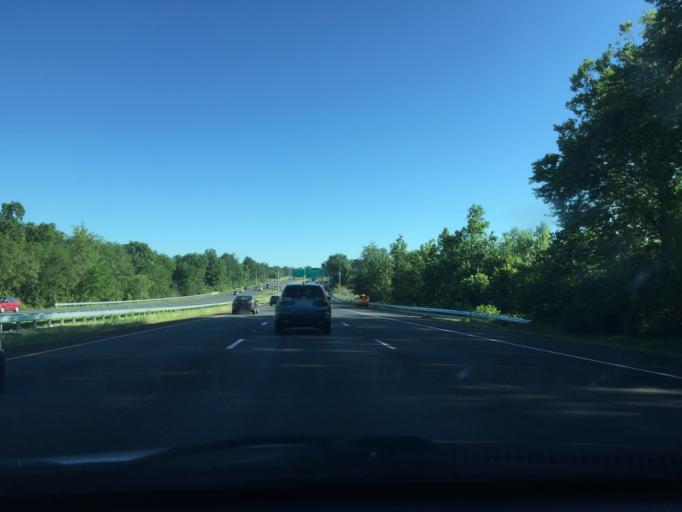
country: US
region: Maryland
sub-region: Baltimore County
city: Cockeysville
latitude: 39.4864
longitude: -76.6659
